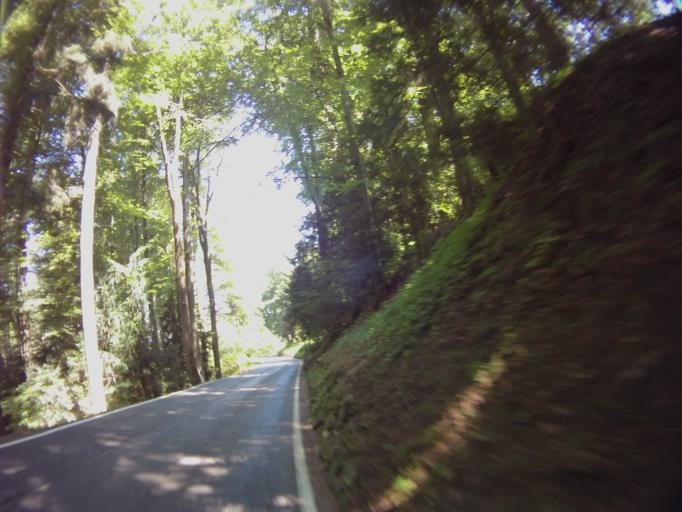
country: CH
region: Schwyz
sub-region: Bezirk Hoefe
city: Freienbach
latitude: 47.1892
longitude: 8.7698
